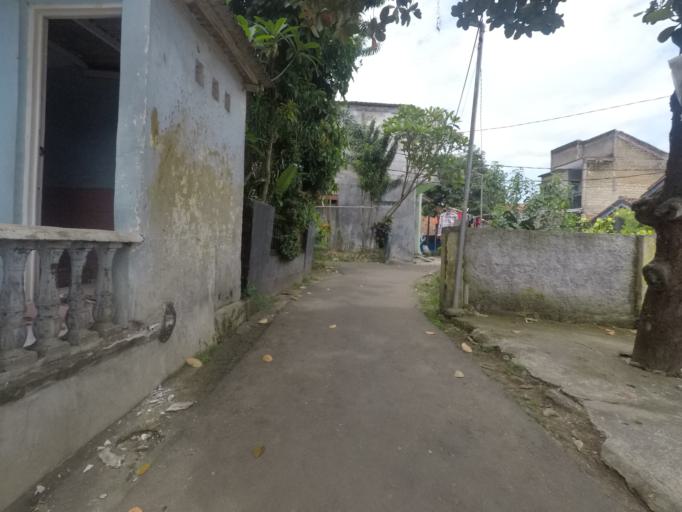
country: ID
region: West Java
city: Ciampea
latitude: -6.5491
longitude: 106.7471
